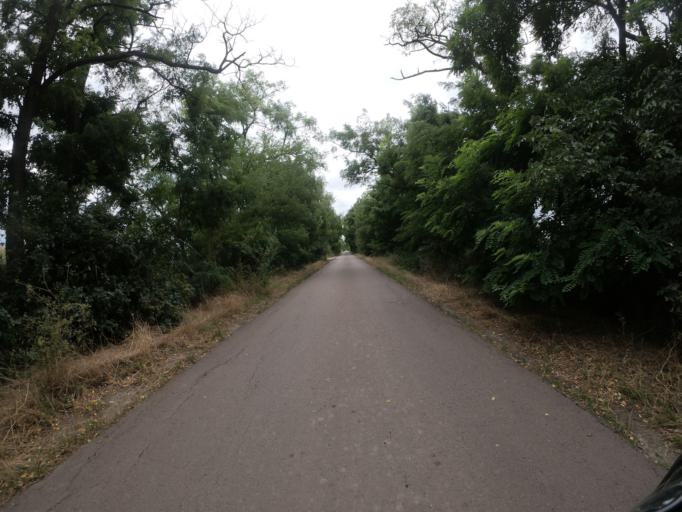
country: HU
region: Borsod-Abauj-Zemplen
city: Szentistvan
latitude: 47.7375
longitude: 20.6822
